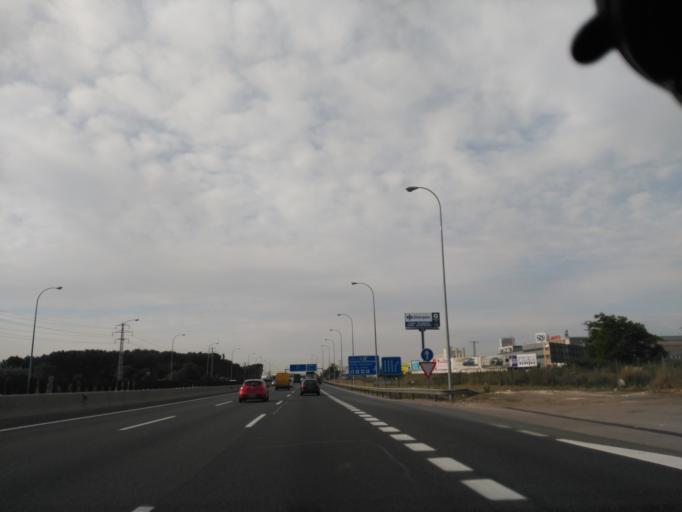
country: ES
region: Madrid
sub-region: Provincia de Madrid
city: Villaverde
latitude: 40.3147
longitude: -3.6922
